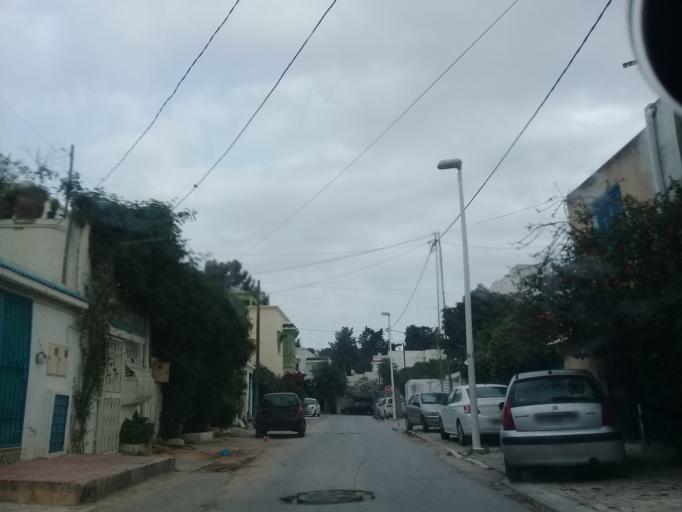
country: TN
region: Tunis
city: Sidi Bou Said
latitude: 36.8687
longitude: 10.3371
